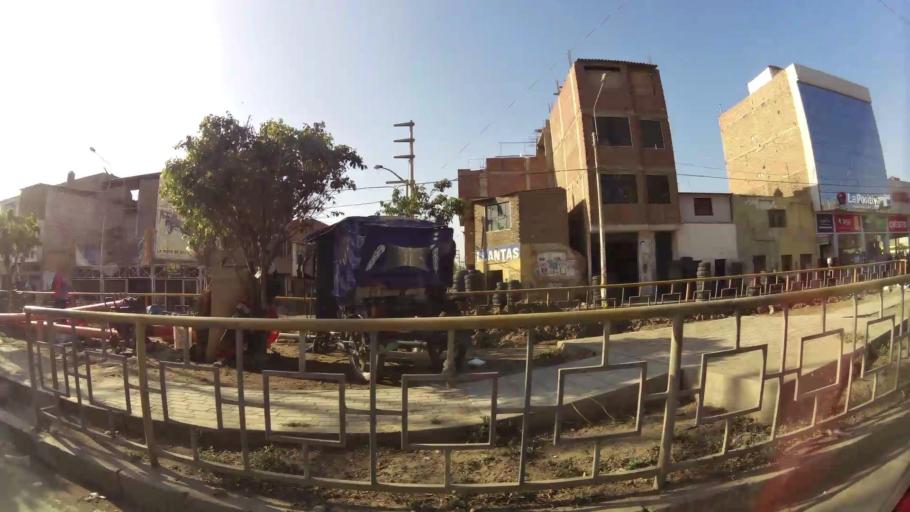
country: PE
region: Lambayeque
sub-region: Provincia de Chiclayo
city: Santa Rosa
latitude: -6.7627
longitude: -79.8395
